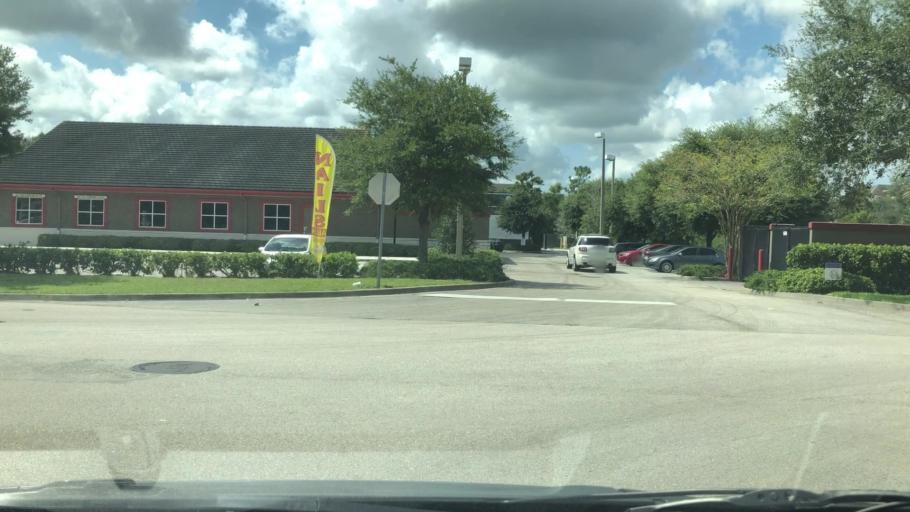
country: US
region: Florida
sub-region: Saint Johns County
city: Fruit Cove
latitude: 30.1400
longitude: -81.5485
